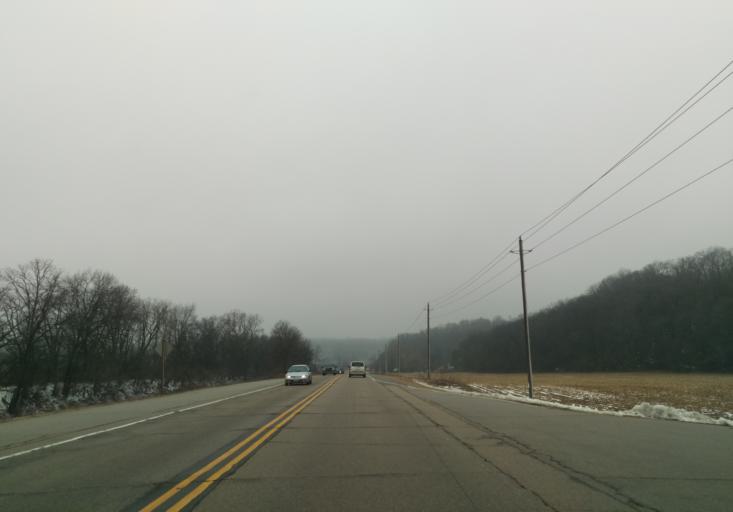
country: US
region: Wisconsin
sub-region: Dane County
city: Middleton
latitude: 43.0930
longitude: -89.5810
